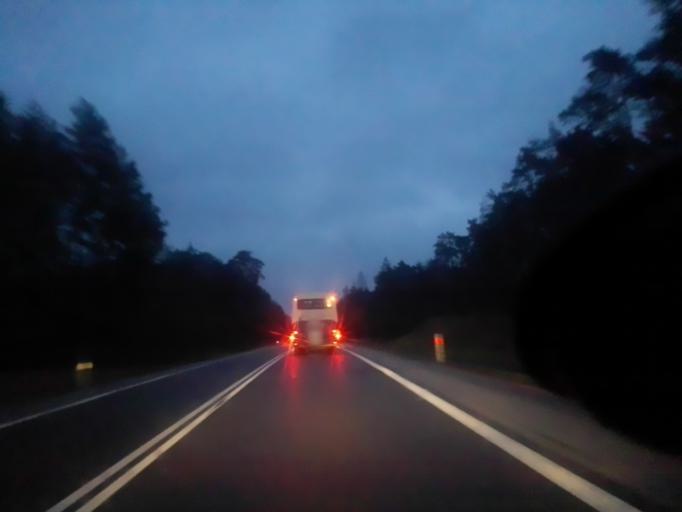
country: PL
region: Masovian Voivodeship
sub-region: Powiat ostrowski
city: Brok
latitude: 52.7261
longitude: 21.7240
